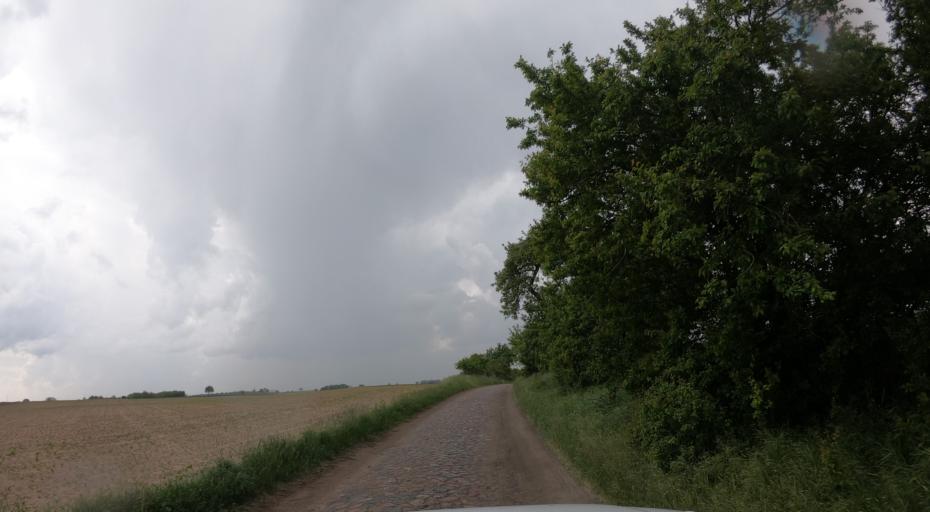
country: PL
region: West Pomeranian Voivodeship
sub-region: Powiat pyrzycki
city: Bielice
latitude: 53.2649
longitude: 14.6947
